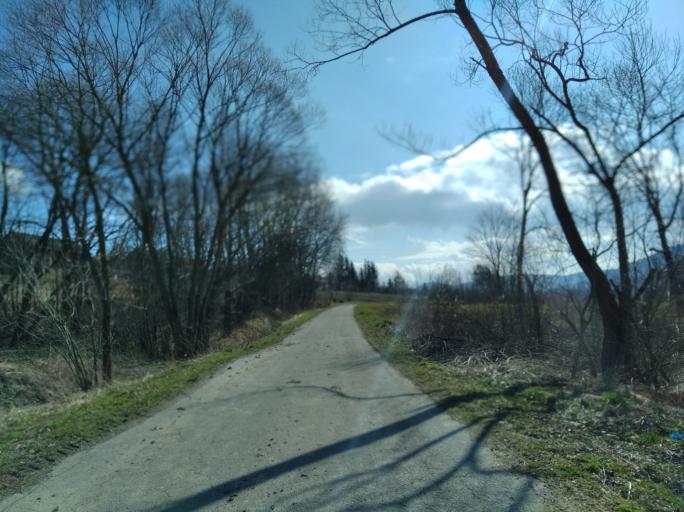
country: PL
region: Subcarpathian Voivodeship
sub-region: Powiat strzyzowski
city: Wysoka Strzyzowska
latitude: 49.8063
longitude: 21.7522
